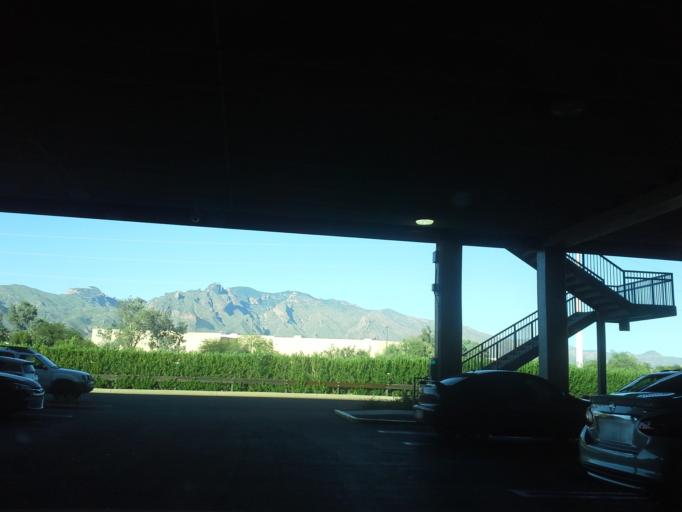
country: US
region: Arizona
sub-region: Pima County
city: Flowing Wells
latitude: 32.2903
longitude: -110.9736
